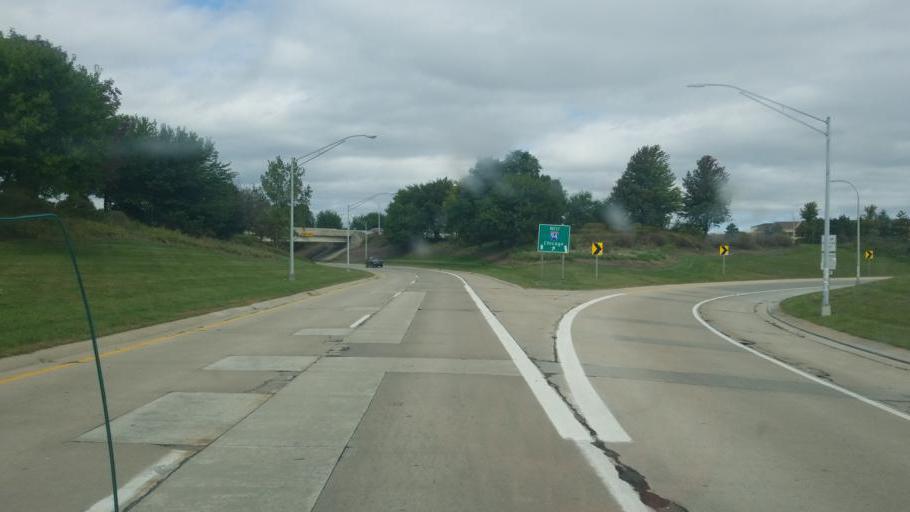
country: US
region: Michigan
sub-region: Wayne County
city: Romulus
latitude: 42.2404
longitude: -83.3420
